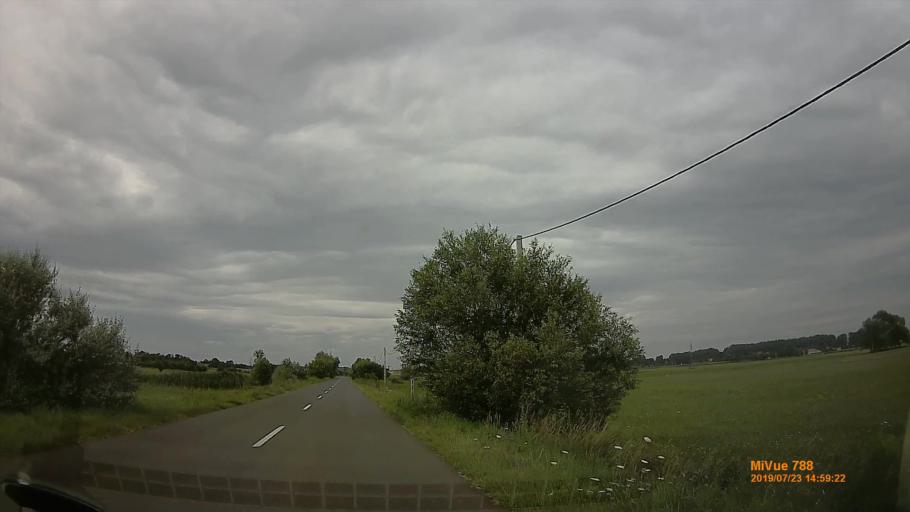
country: HU
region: Szabolcs-Szatmar-Bereg
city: Nyiregyhaza
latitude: 47.9202
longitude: 21.6768
